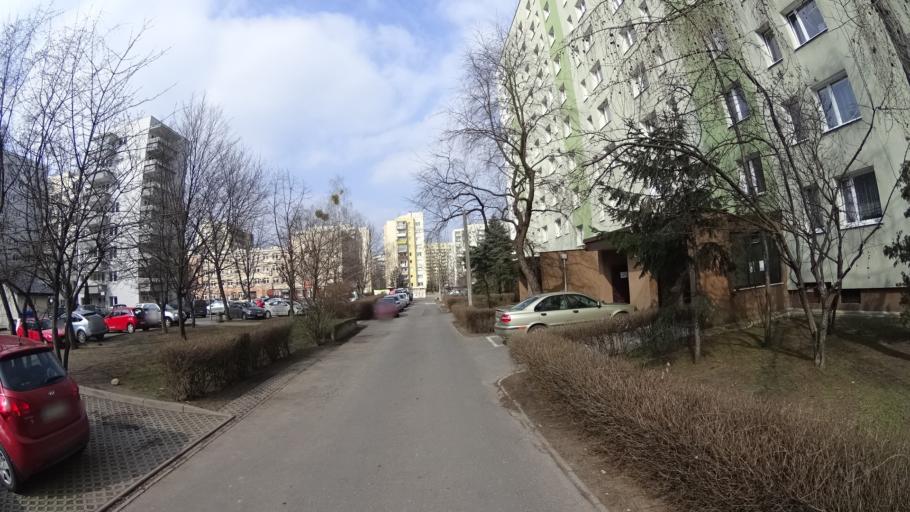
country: PL
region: Masovian Voivodeship
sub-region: Warszawa
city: Bemowo
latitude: 52.2507
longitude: 20.9258
